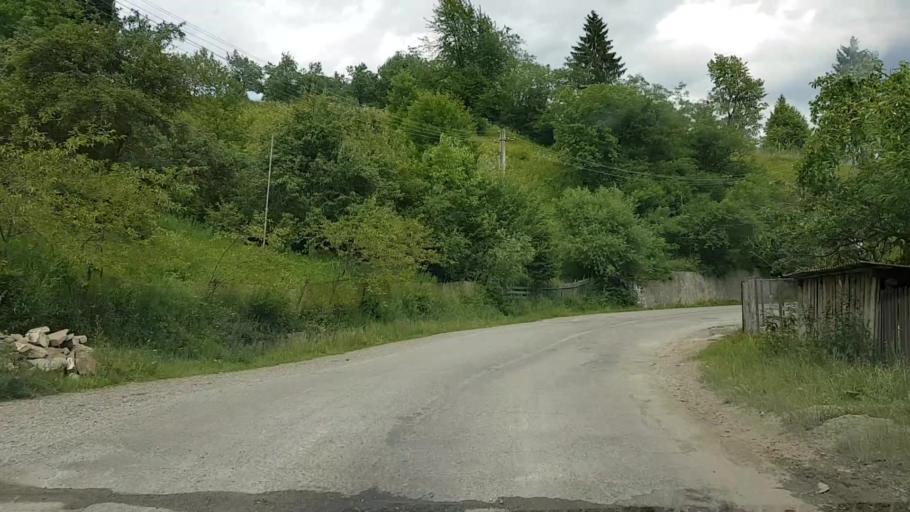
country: RO
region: Neamt
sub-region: Comuna Hangu
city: Hangu
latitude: 47.0538
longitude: 26.0242
